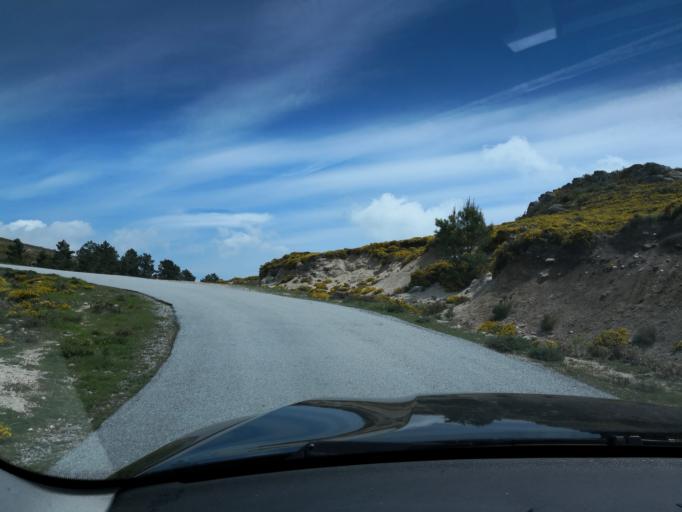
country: PT
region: Vila Real
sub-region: Vila Real
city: Vila Real
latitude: 41.3244
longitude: -7.7899
